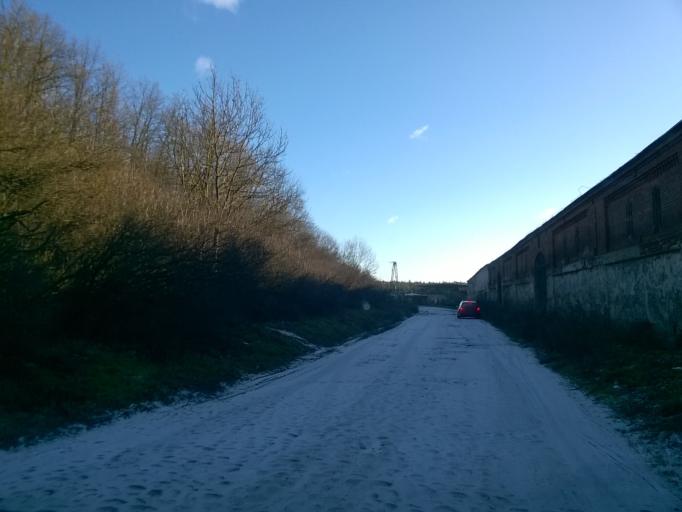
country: PL
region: Kujawsko-Pomorskie
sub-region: Powiat nakielski
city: Sadki
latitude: 53.1421
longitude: 17.4420
